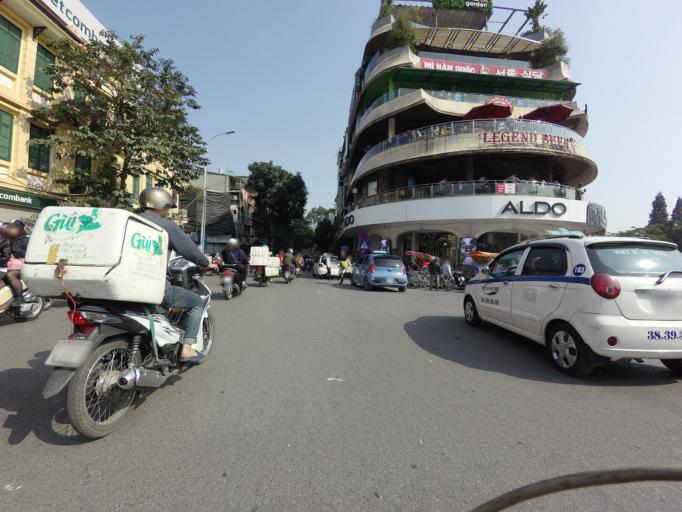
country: VN
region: Ha Noi
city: Hoan Kiem
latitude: 21.0323
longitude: 105.8516
